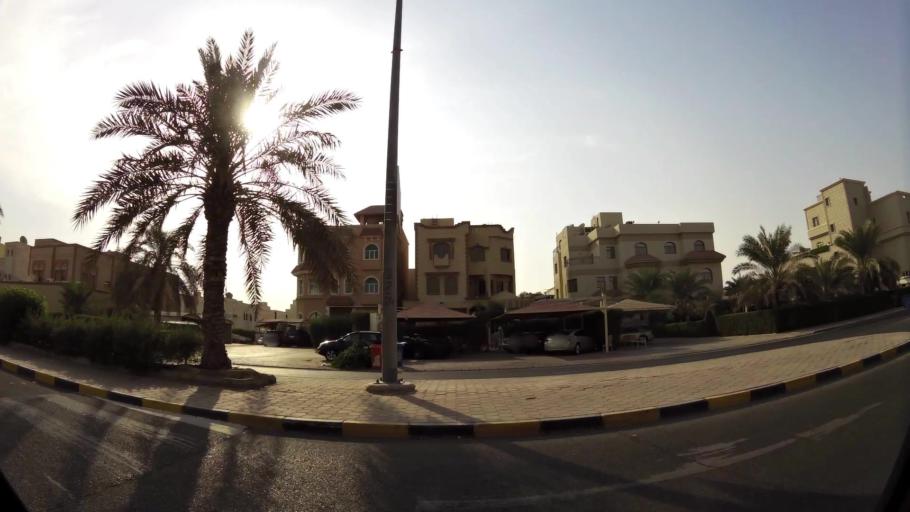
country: KW
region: Muhafazat Hawalli
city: Hawalli
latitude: 29.3250
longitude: 47.9979
